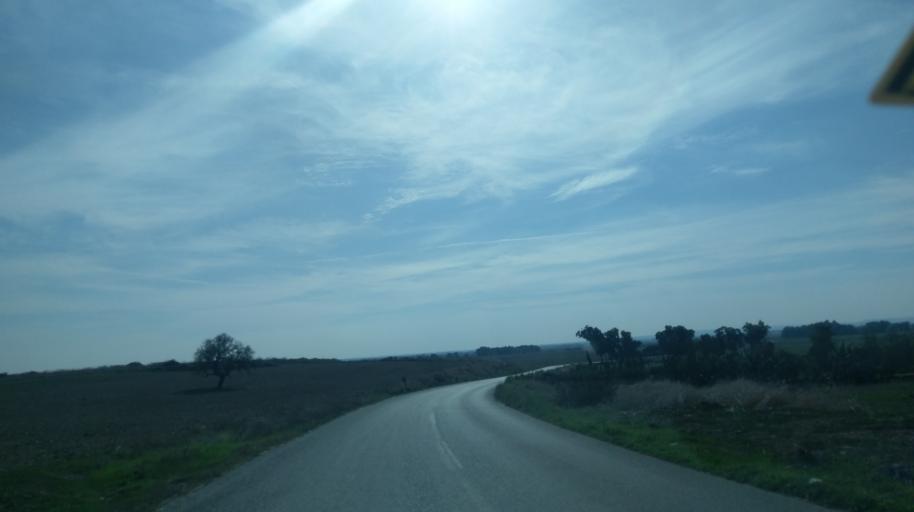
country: CY
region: Ammochostos
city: Lefkonoiko
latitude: 35.2143
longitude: 33.6987
